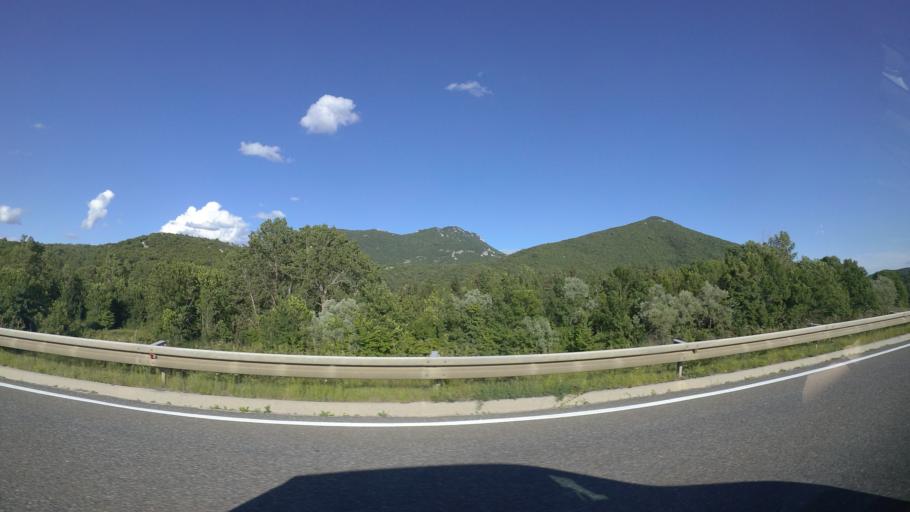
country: HR
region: Zadarska
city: Gracac
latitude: 44.4555
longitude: 15.6698
